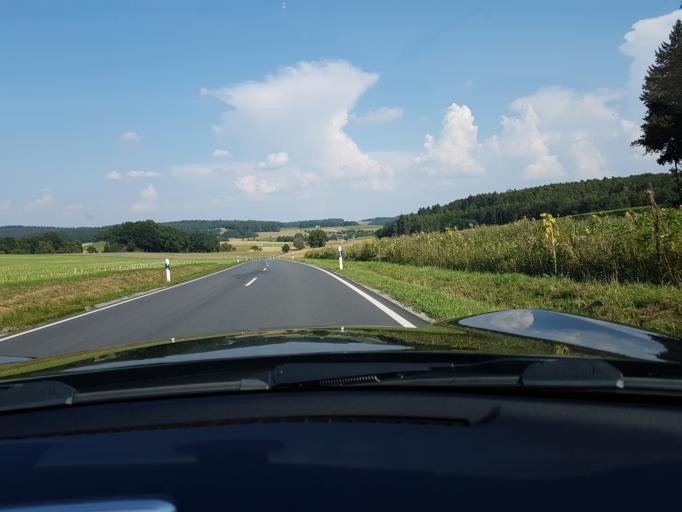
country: DE
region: Baden-Wuerttemberg
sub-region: Karlsruhe Region
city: Osterburken
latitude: 49.4765
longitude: 9.3905
